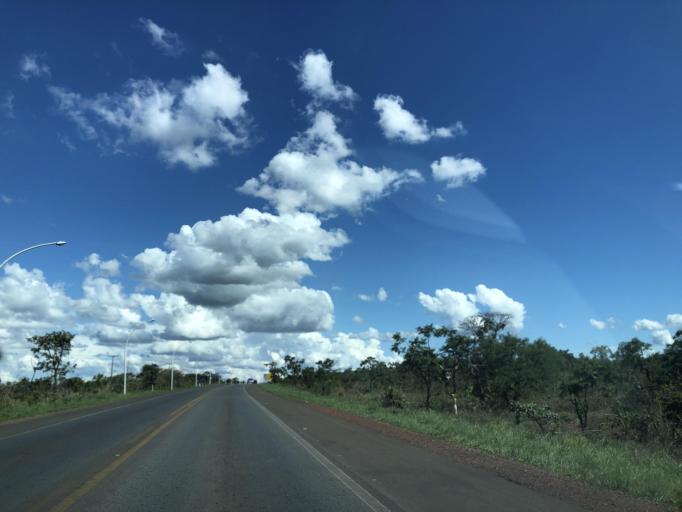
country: BR
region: Federal District
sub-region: Brasilia
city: Brasilia
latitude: -15.6676
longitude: -47.8840
